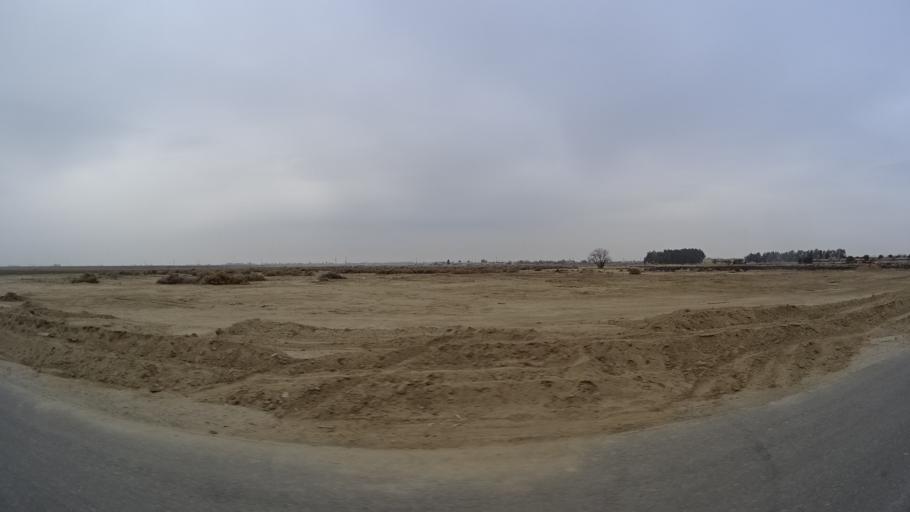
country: US
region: California
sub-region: Kern County
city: Bakersfield
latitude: 35.3443
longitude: -118.9496
